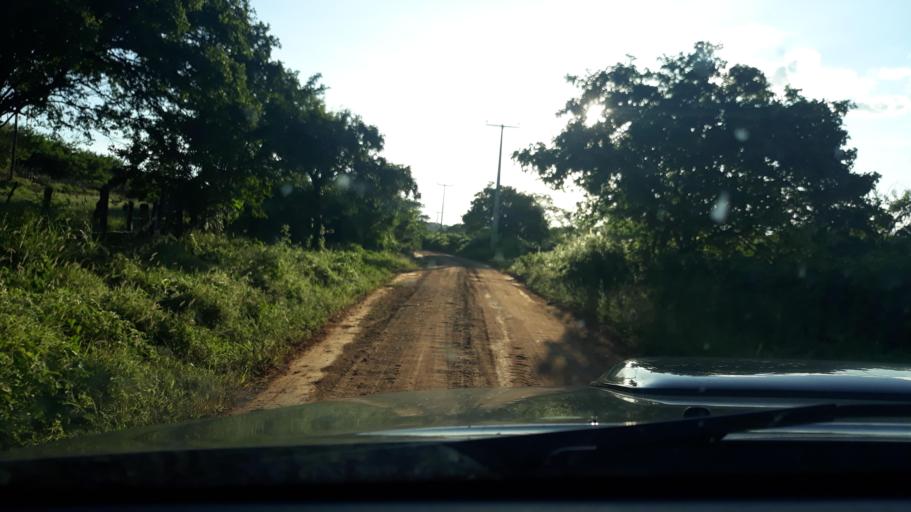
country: BR
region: Bahia
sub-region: Riacho De Santana
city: Riacho de Santana
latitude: -13.8464
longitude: -42.7442
